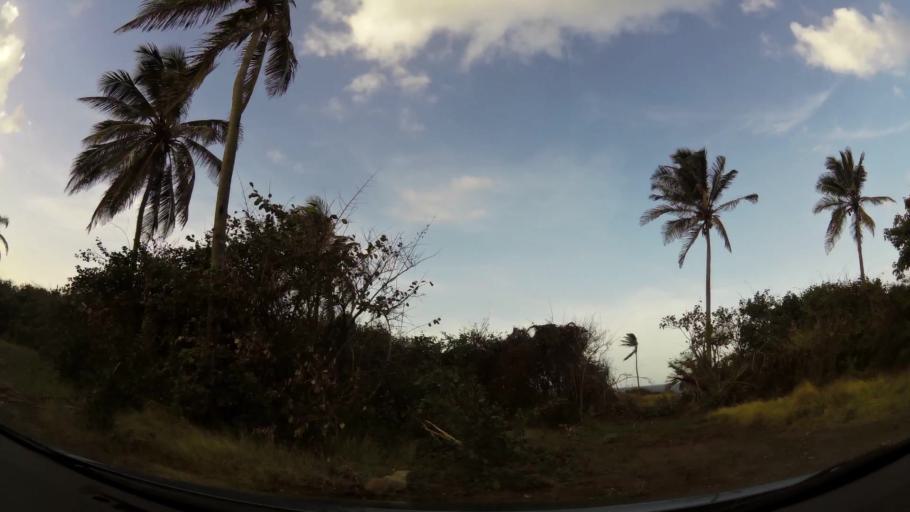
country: KN
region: Saint James Windwa
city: Newcastle
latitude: 17.1944
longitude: -62.5603
